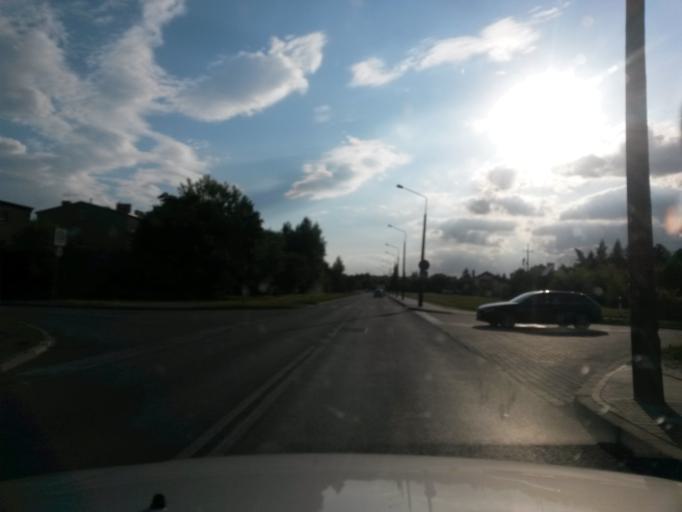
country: PL
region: Lodz Voivodeship
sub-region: Powiat belchatowski
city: Belchatow
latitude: 51.3704
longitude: 19.3626
